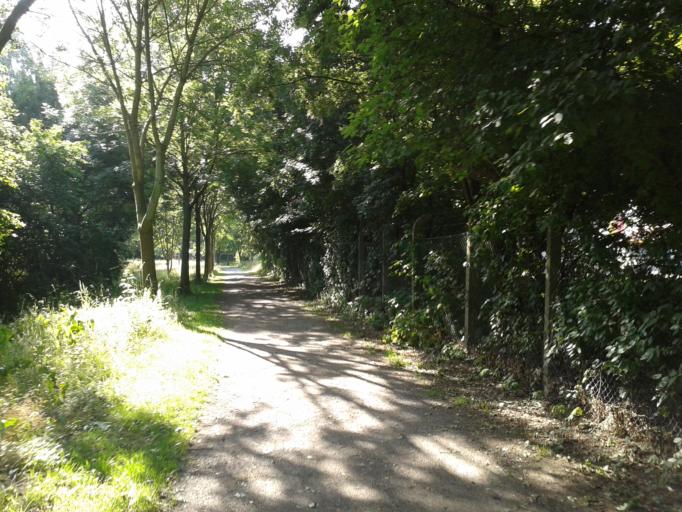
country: DE
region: North Rhine-Westphalia
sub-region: Regierungsbezirk Detmold
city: Hovelhof
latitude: 51.7471
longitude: 8.6742
